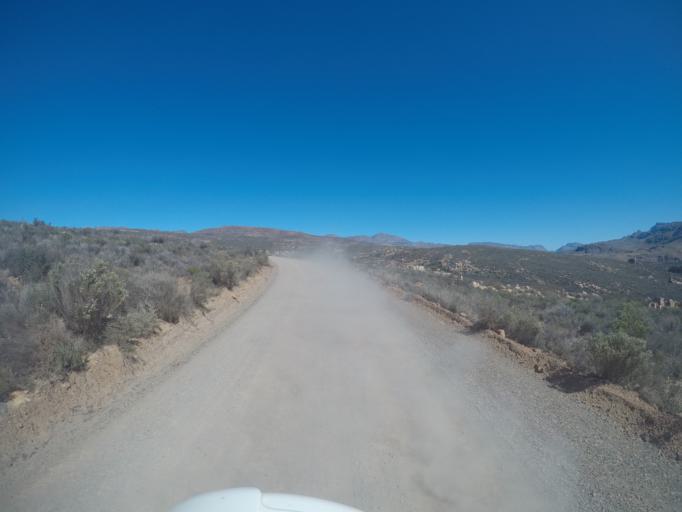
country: ZA
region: Western Cape
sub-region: West Coast District Municipality
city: Clanwilliam
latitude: -32.5062
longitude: 19.3011
